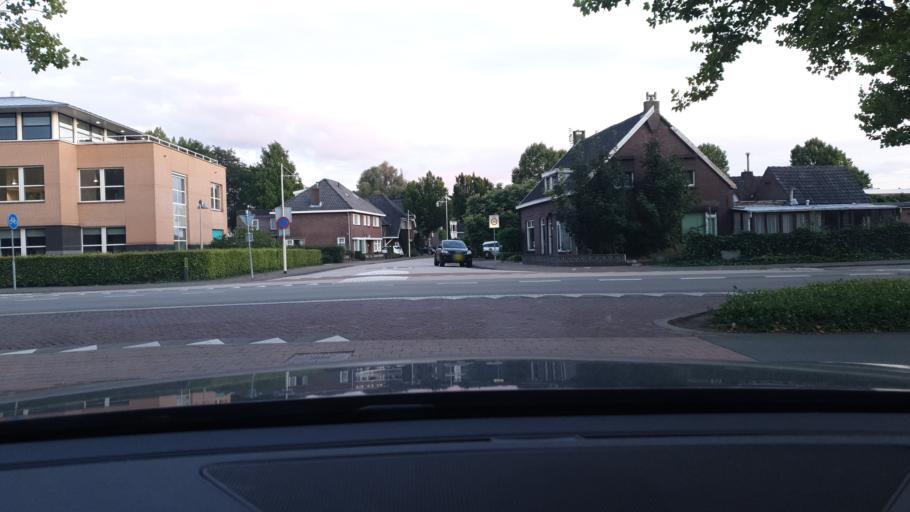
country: NL
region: North Brabant
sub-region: Gemeente Waalre
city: Waalre
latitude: 51.4018
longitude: 5.4759
